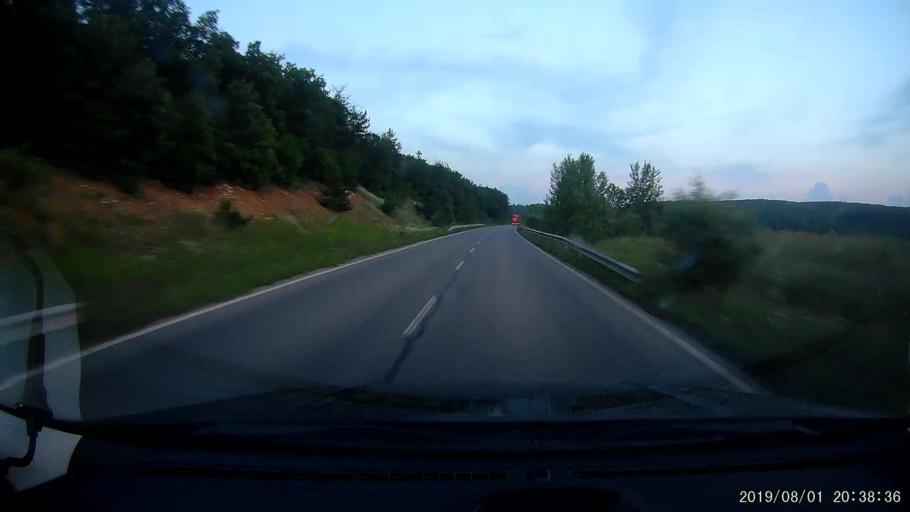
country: BG
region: Yambol
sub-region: Obshtina Elkhovo
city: Elkhovo
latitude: 42.0224
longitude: 26.6020
